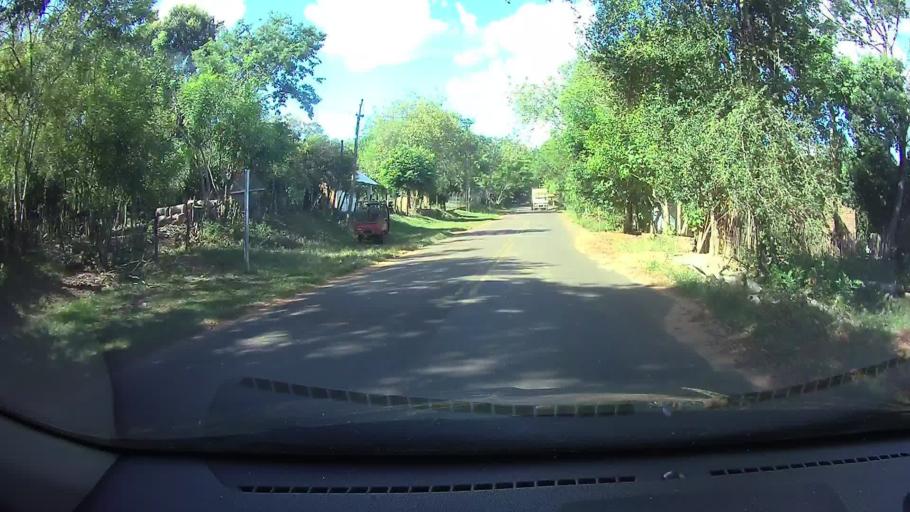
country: PY
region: Paraguari
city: Sapucai
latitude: -25.6708
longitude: -56.8618
